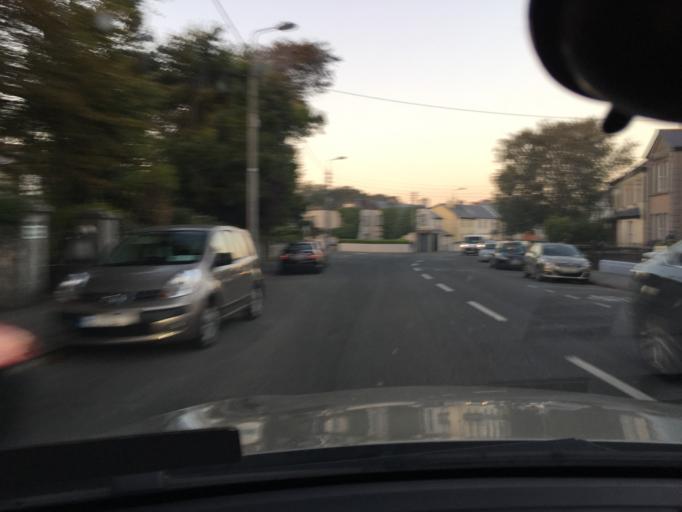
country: IE
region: Connaught
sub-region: County Galway
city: Gaillimh
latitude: 53.2648
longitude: -9.0724
